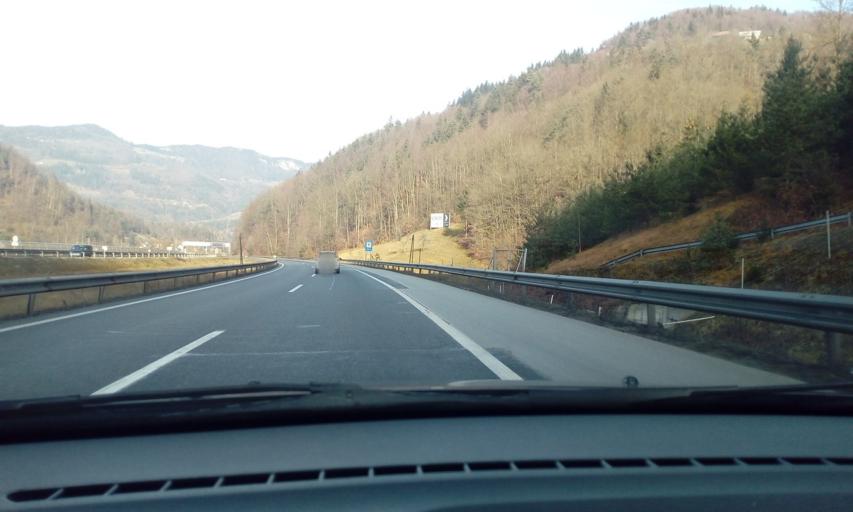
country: SI
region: Vransko
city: Vransko
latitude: 46.2269
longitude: 14.9464
